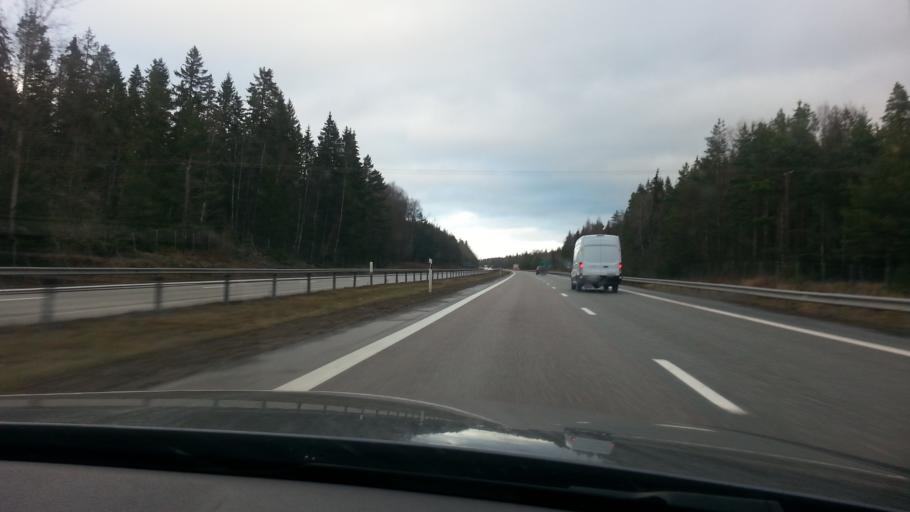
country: SE
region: Joenkoeping
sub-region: Jonkopings Kommun
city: Asa
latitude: 58.1013
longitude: 14.5556
